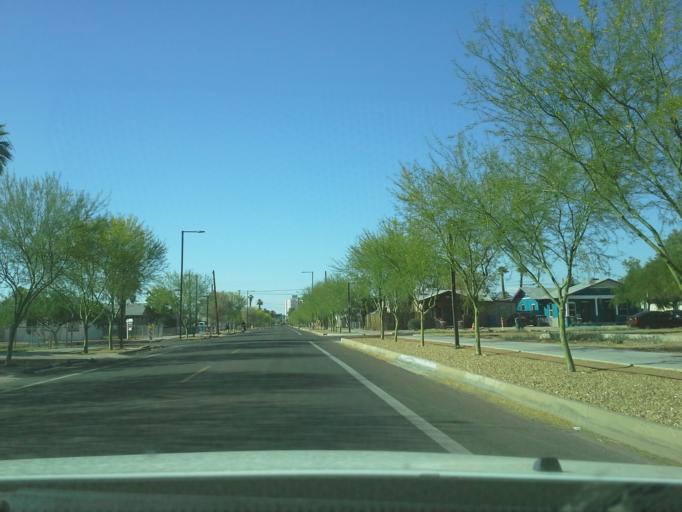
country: US
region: Arizona
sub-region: Maricopa County
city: Phoenix
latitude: 33.4534
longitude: -112.0589
